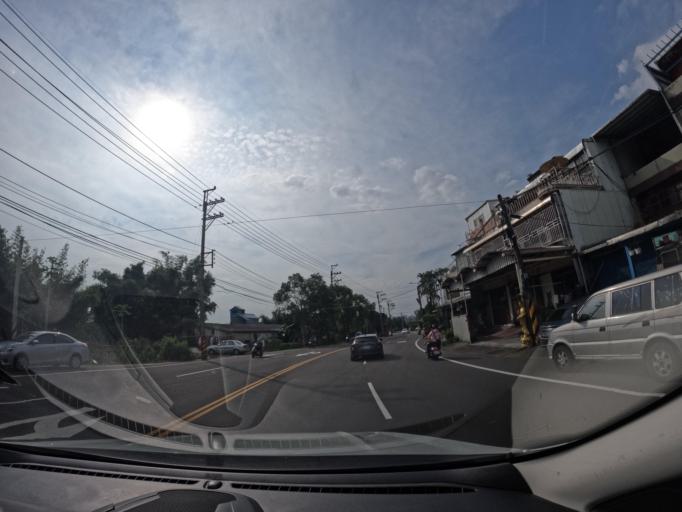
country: TW
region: Taiwan
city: Daxi
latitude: 24.8946
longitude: 121.3035
